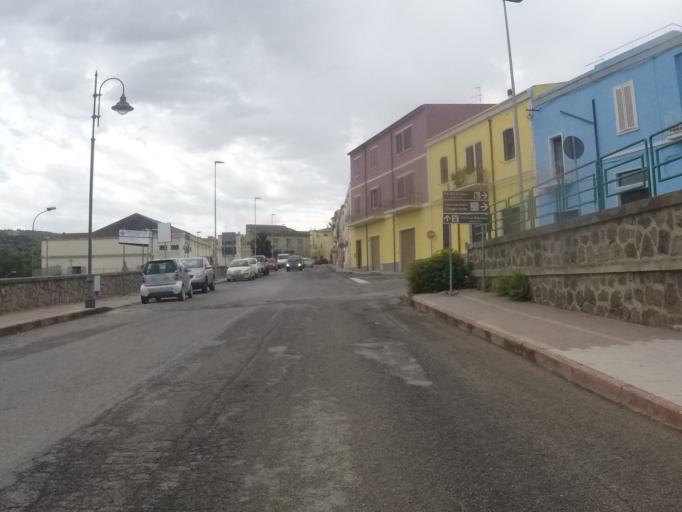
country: IT
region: Sardinia
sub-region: Provincia di Sassari
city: Sorso
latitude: 40.8012
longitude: 8.5808
